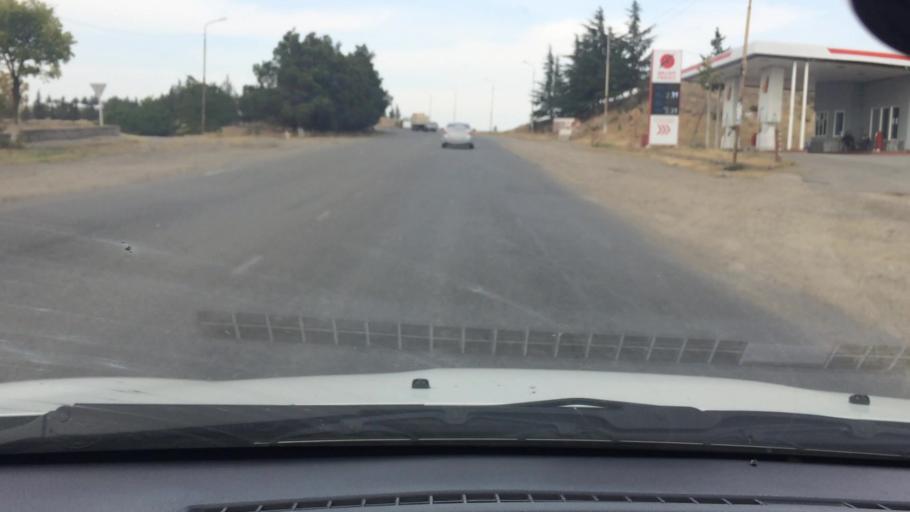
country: GE
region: Kvemo Kartli
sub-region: Marneuli
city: Marneuli
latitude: 41.4980
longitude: 44.8029
